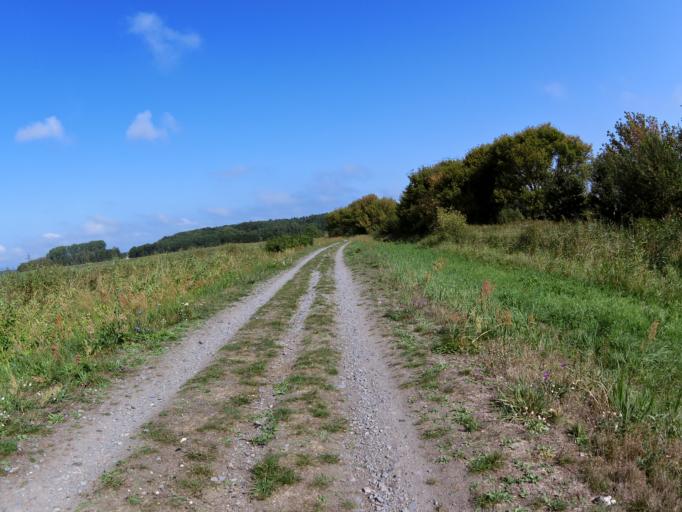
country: DE
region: Mecklenburg-Vorpommern
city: Loddin
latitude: 53.9939
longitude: 14.0474
